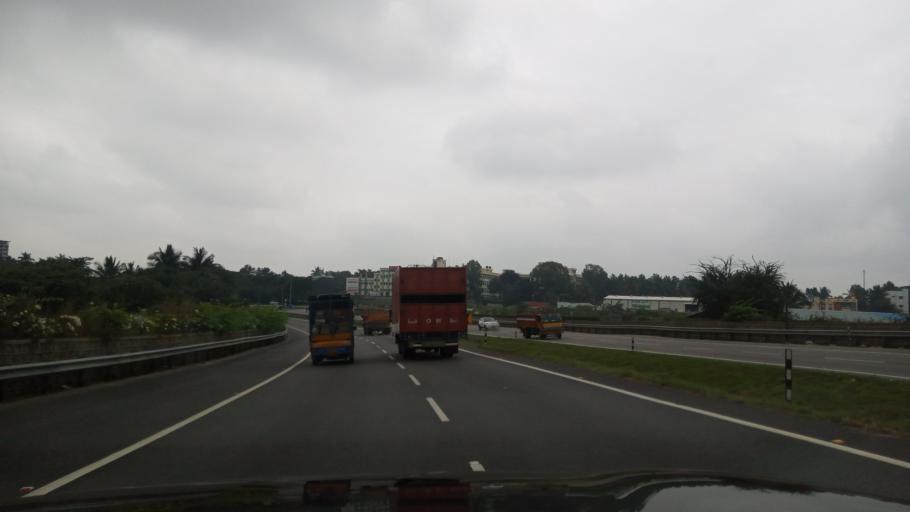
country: IN
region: Karnataka
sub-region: Bangalore Urban
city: Bangalore
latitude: 12.8502
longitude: 77.5899
